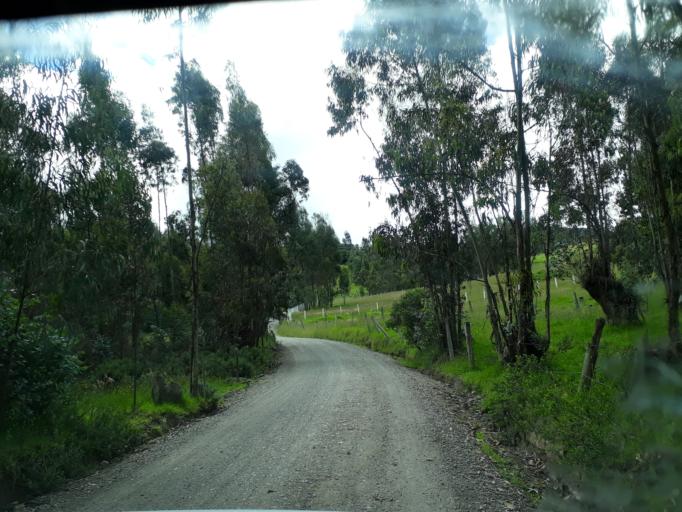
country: CO
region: Cundinamarca
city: La Mesa
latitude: 5.2800
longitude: -73.9086
